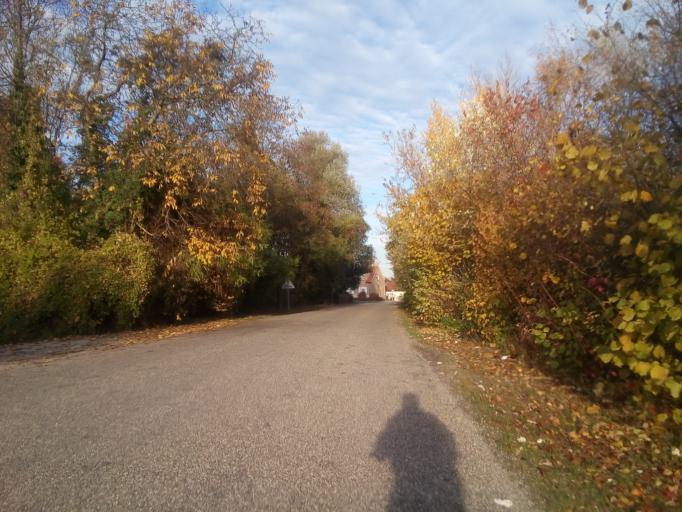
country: FR
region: Alsace
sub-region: Departement du Bas-Rhin
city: Herrlisheim
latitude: 48.7066
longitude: 7.9169
